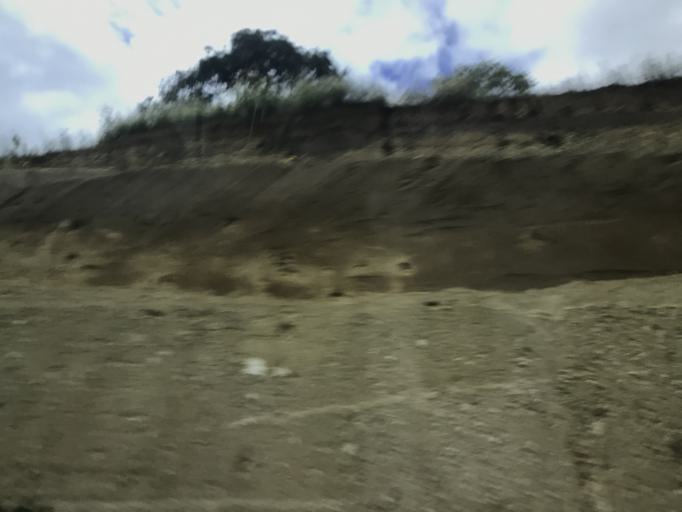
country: GT
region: Chimaltenango
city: El Tejar
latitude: 14.6322
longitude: -90.7917
